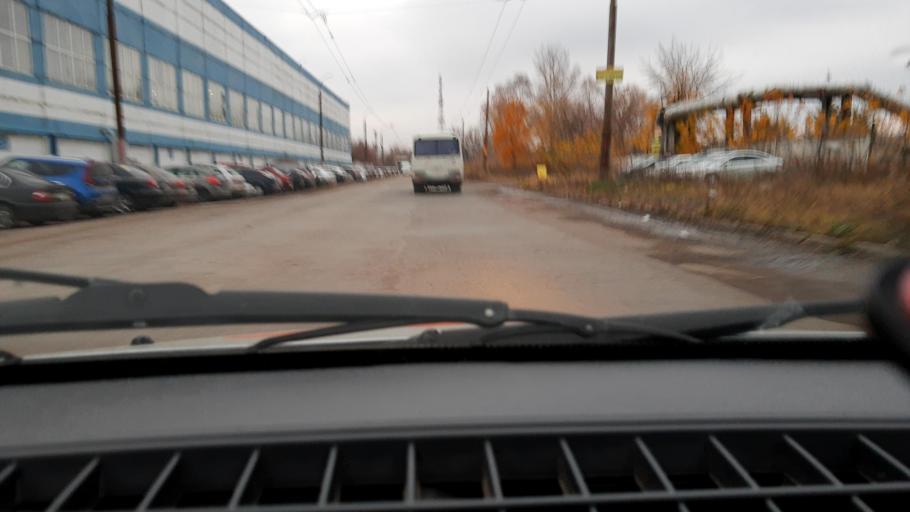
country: RU
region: Bashkortostan
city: Ufa
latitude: 54.8292
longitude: 56.1163
